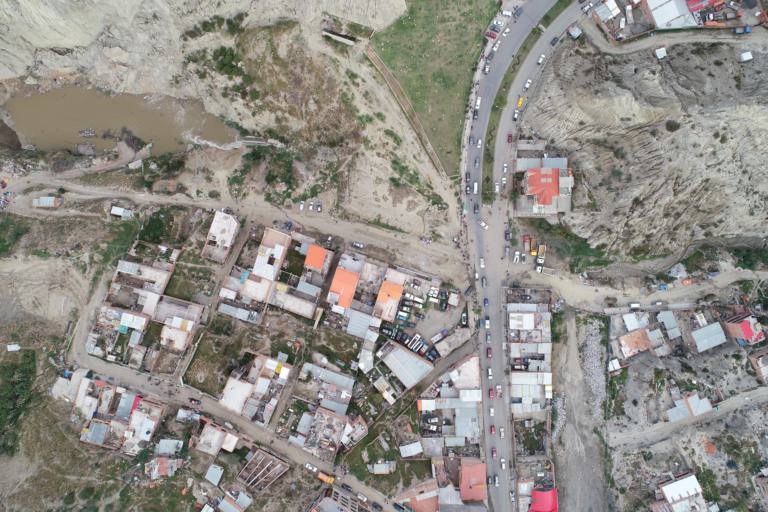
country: BO
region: La Paz
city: La Paz
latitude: -16.5214
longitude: -68.1228
